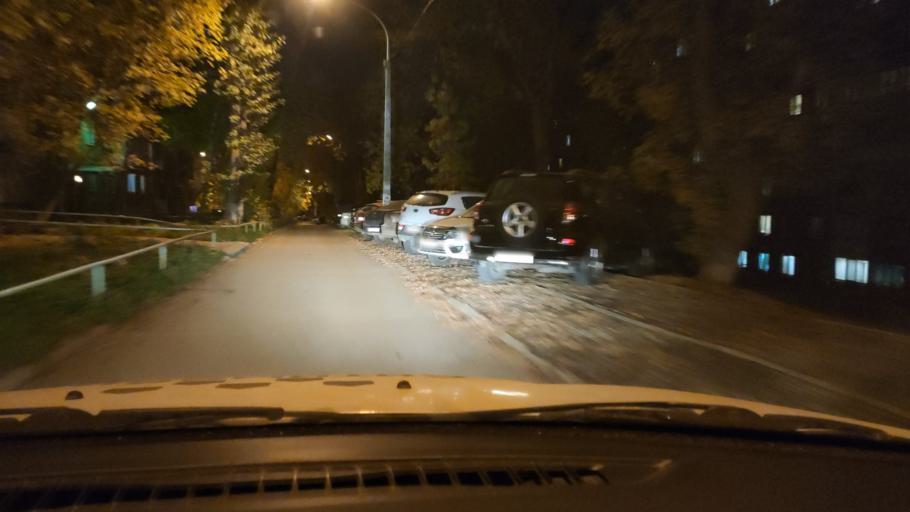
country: RU
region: Perm
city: Perm
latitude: 57.9773
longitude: 56.2369
